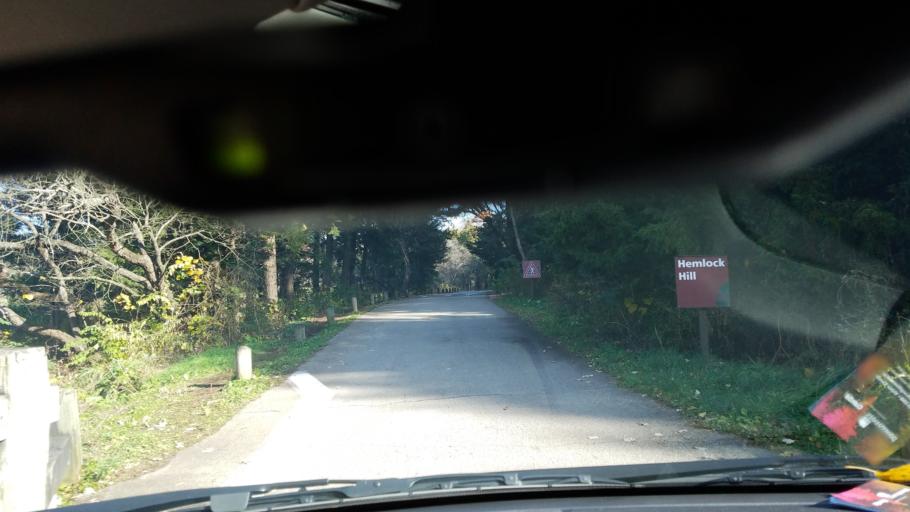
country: US
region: Illinois
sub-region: DuPage County
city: Lisle
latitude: 41.8156
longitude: -88.0843
